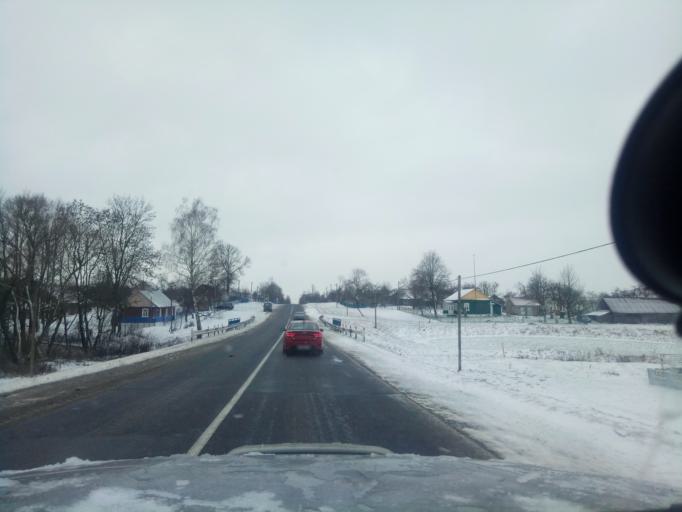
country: BY
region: Minsk
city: Klyetsk
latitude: 53.1318
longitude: 26.6726
